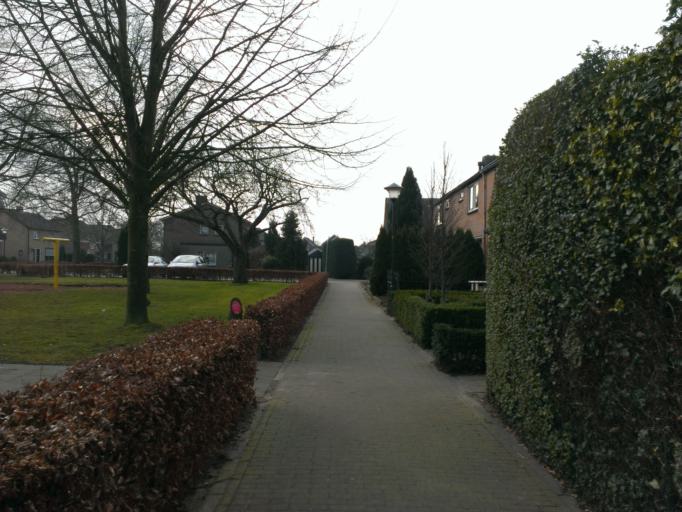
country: NL
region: Gelderland
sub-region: Gemeente Voorst
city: Twello
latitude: 52.2351
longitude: 6.0939
